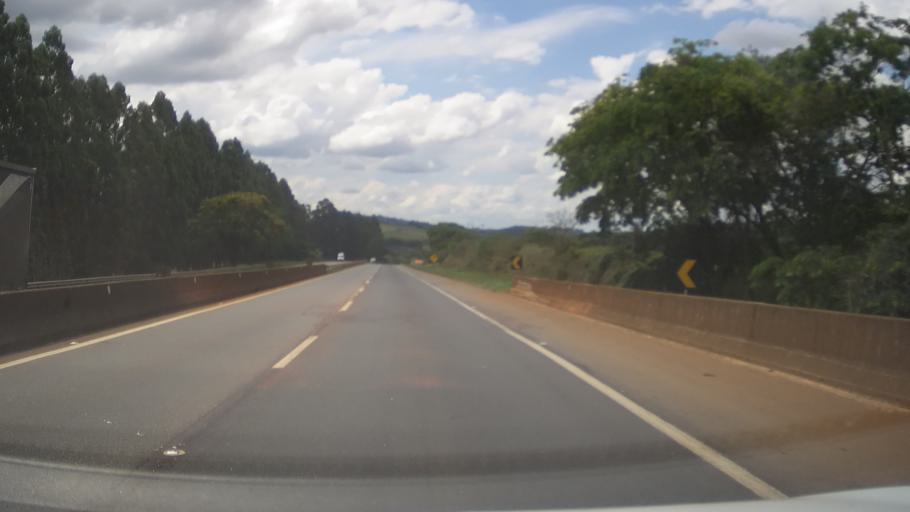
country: BR
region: Minas Gerais
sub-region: Nepomuceno
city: Nepomuceno
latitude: -21.2414
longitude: -45.1354
